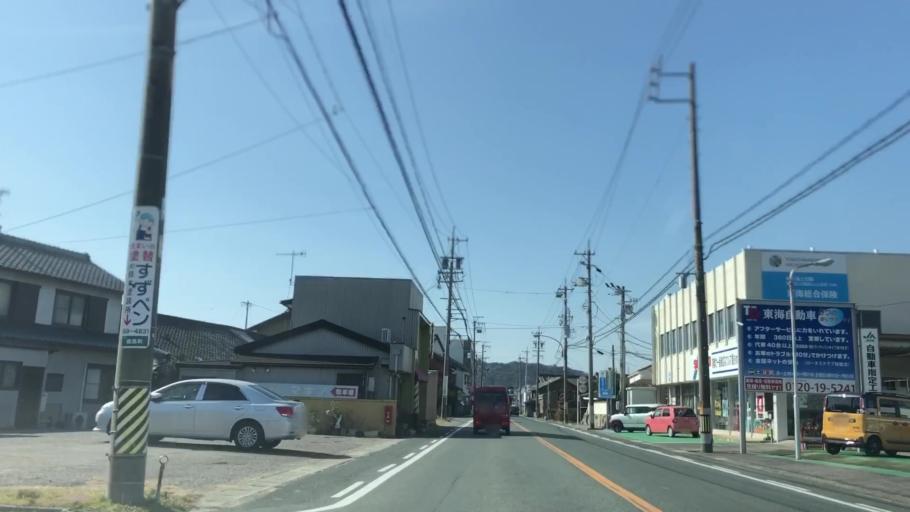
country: JP
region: Aichi
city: Gamagori
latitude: 34.8146
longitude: 137.1918
